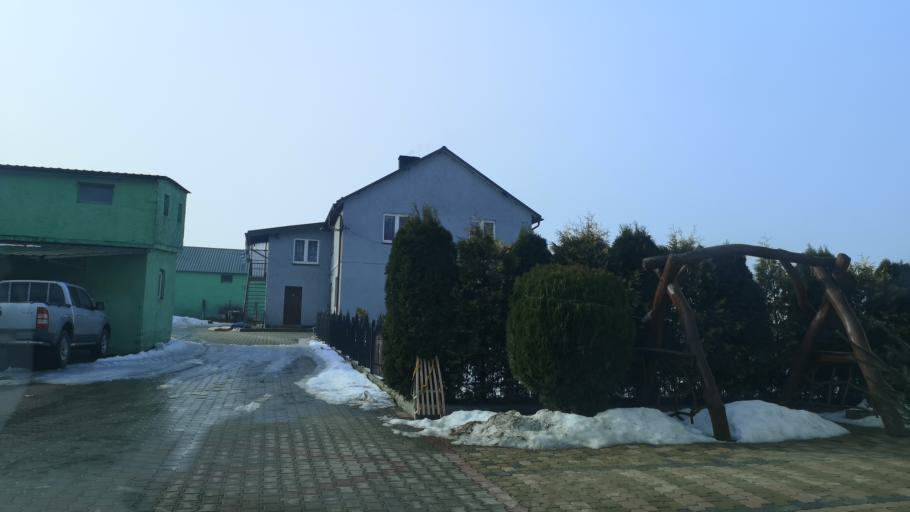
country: PL
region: Warmian-Masurian Voivodeship
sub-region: Powiat nowomiejski
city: Biskupiec
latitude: 53.5455
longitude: 19.3576
